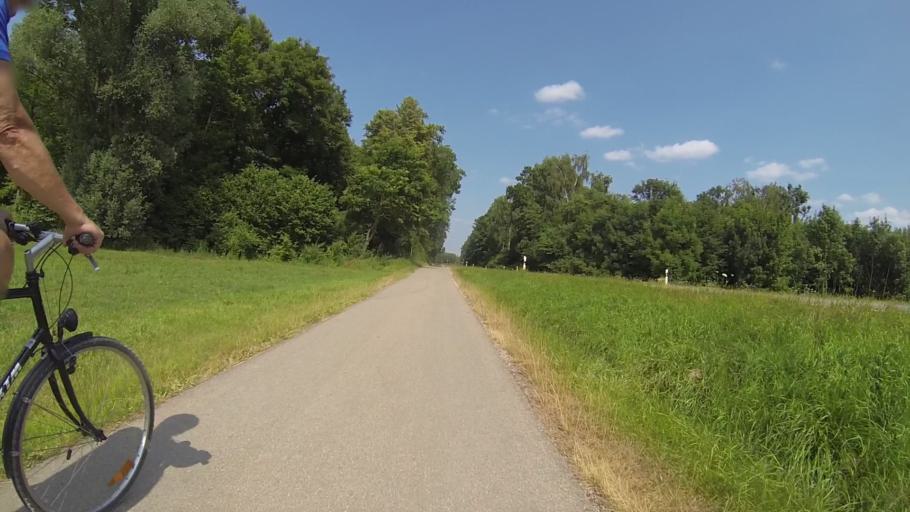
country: DE
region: Bavaria
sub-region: Swabia
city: Guenzburg
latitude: 48.4817
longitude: 10.2921
